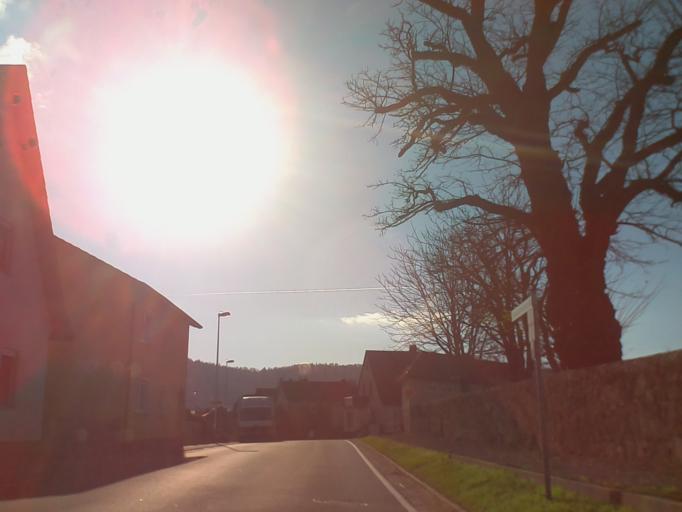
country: DE
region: Bavaria
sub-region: Regierungsbezirk Unterfranken
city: Bad Bocklet
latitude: 50.2885
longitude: 10.0992
